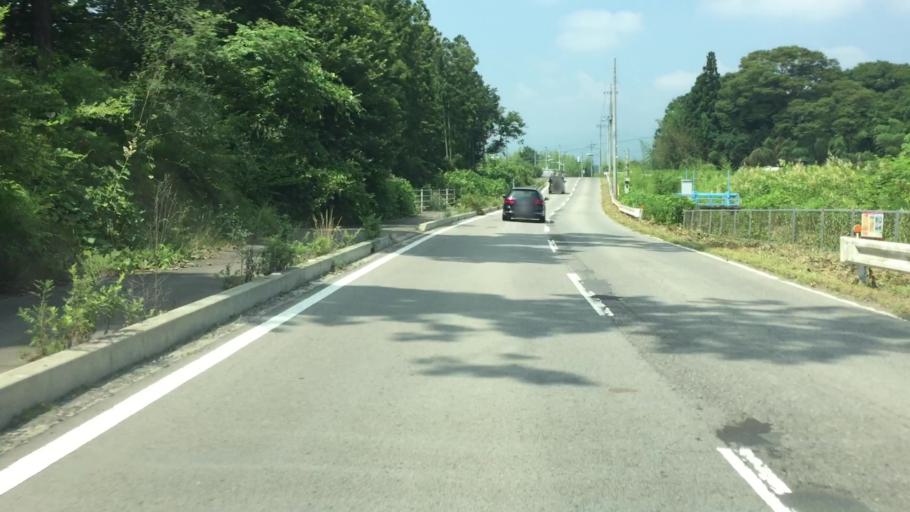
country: JP
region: Tochigi
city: Kuroiso
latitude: 36.9758
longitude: 139.9724
